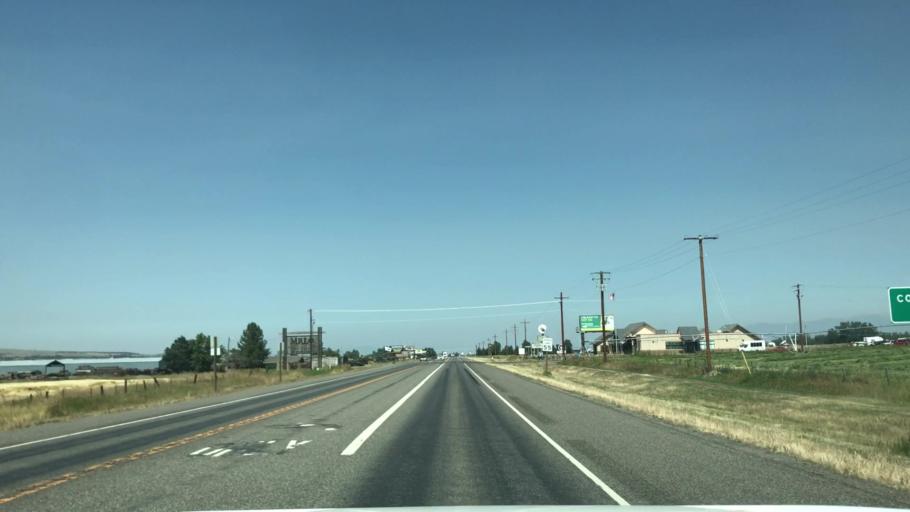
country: US
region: Montana
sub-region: Gallatin County
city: Four Corners
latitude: 45.5822
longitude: -111.1970
